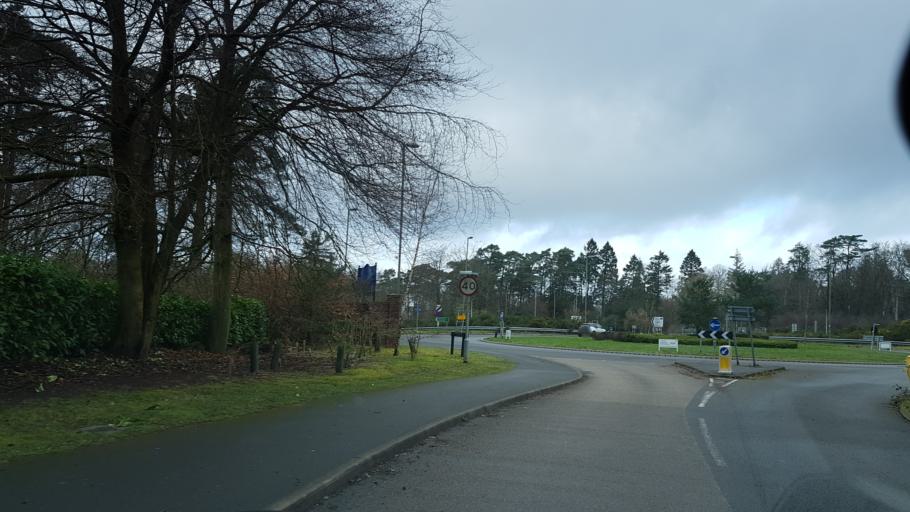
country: GB
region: England
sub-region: Surrey
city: Hindhead
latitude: 51.1054
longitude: -0.7419
